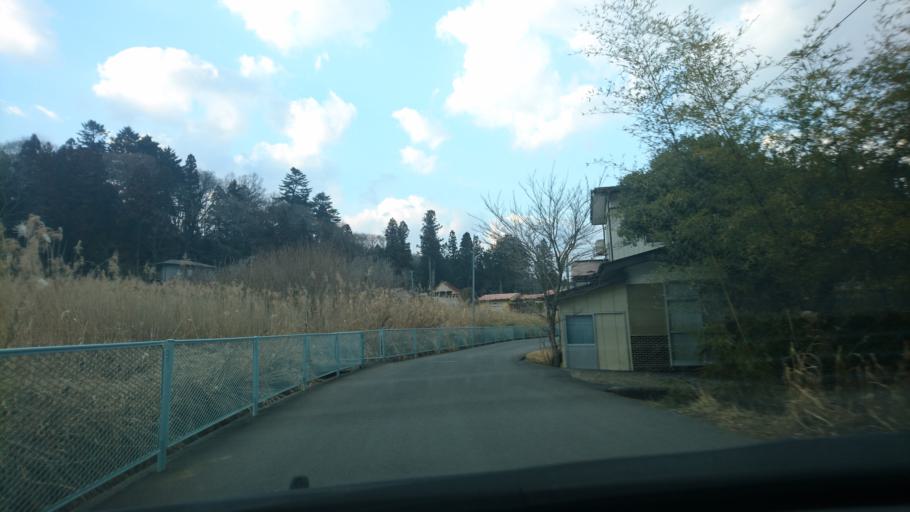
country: JP
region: Iwate
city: Ichinoseki
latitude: 38.9465
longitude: 141.1287
